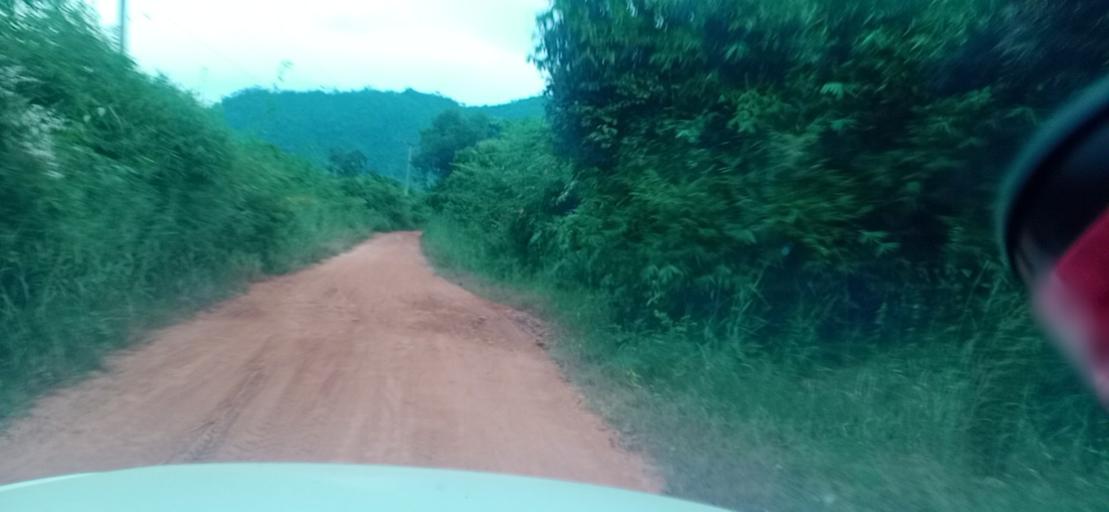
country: TH
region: Changwat Bueng Kan
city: Pak Khat
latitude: 18.5621
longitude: 103.2983
